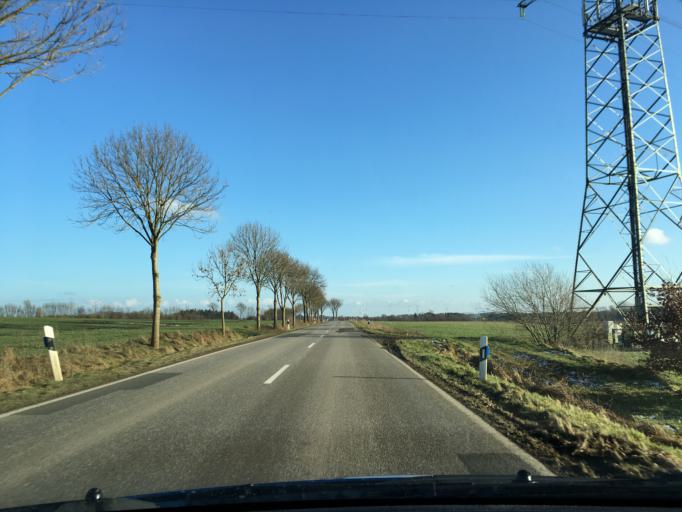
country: DE
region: Schleswig-Holstein
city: Gulzow
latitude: 53.4442
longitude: 10.5186
